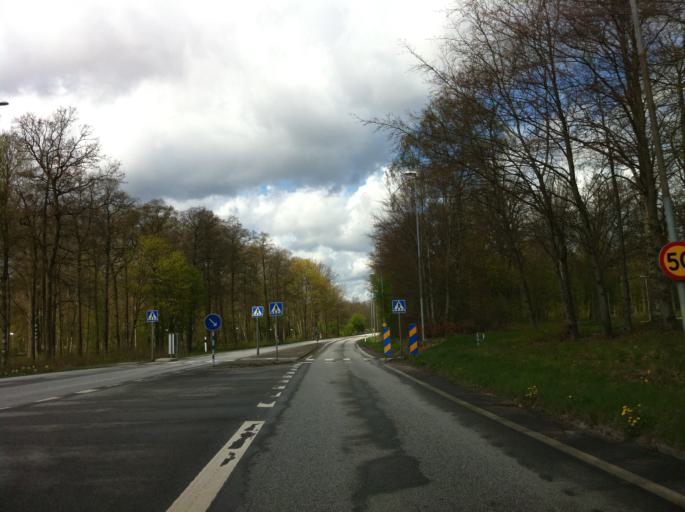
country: SE
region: Skane
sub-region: Hoors Kommun
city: Satofta
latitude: 55.9316
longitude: 13.5627
